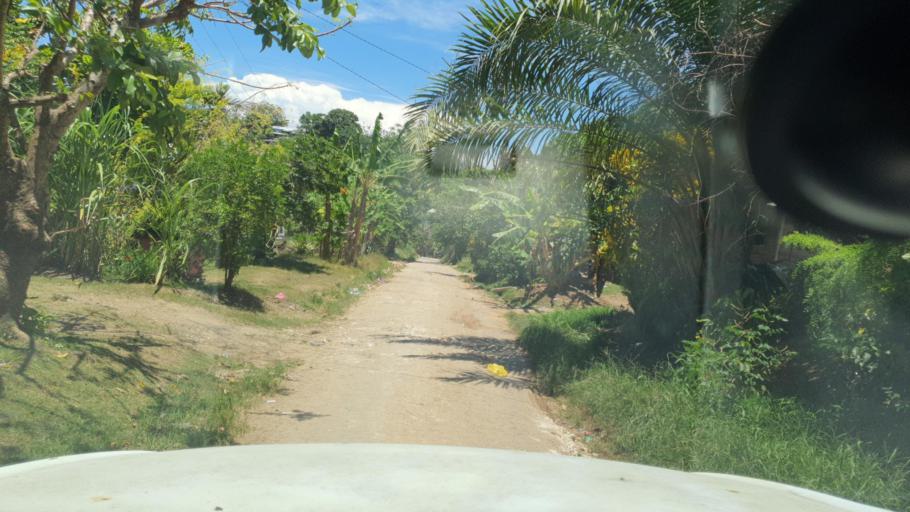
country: SB
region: Guadalcanal
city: Honiara
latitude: -9.4404
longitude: 159.9876
